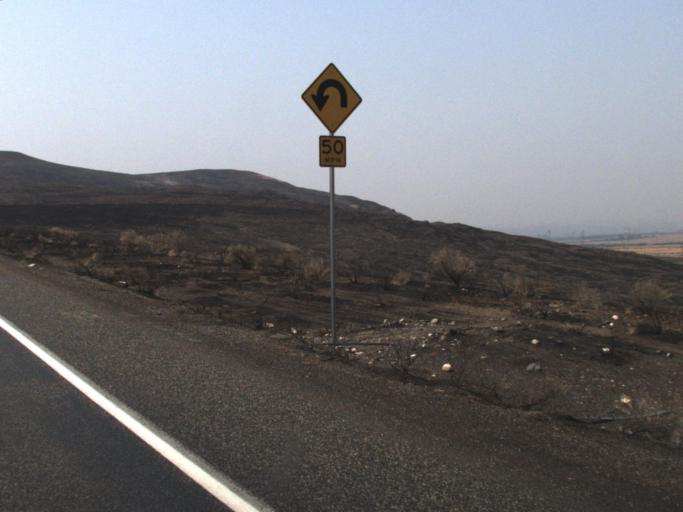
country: US
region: Washington
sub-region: Grant County
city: Desert Aire
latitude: 46.6110
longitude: -119.7319
